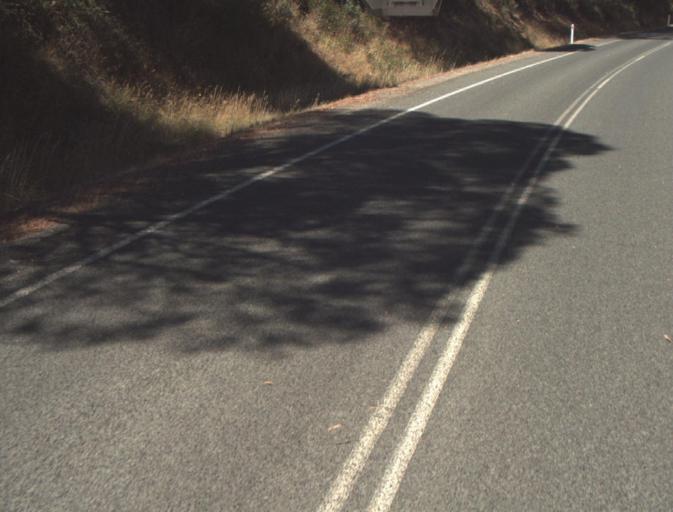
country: AU
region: Tasmania
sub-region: Dorset
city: Scottsdale
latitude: -41.3118
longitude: 147.3681
